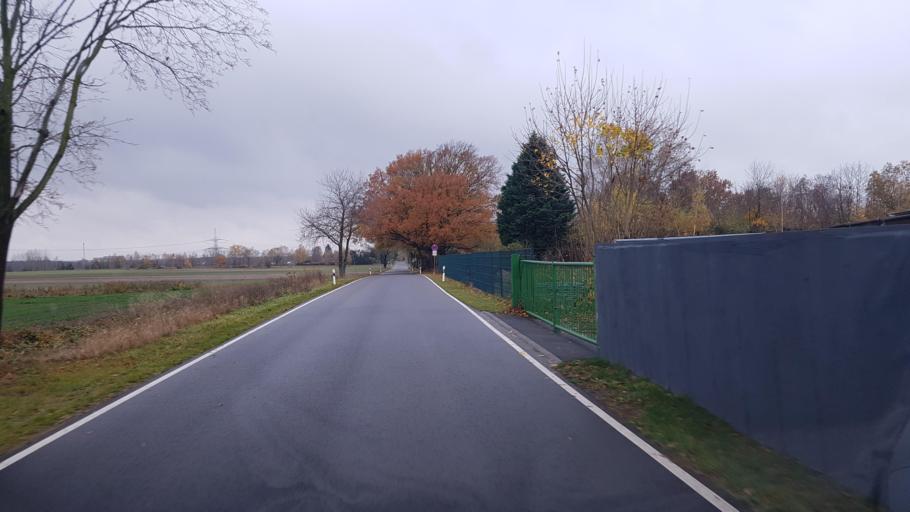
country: DE
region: Brandenburg
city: Drebkau
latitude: 51.6624
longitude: 14.2560
